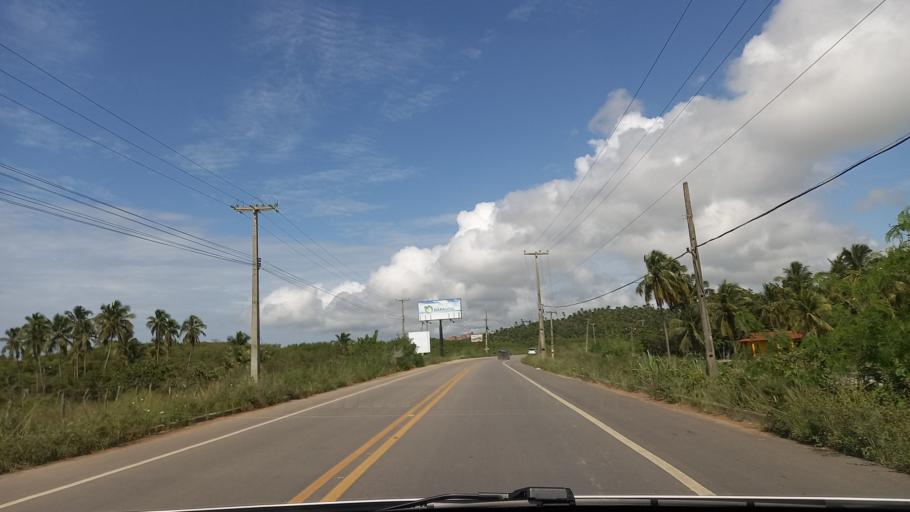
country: BR
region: Alagoas
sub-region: Maragogi
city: Maragogi
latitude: -8.9943
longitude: -35.2084
